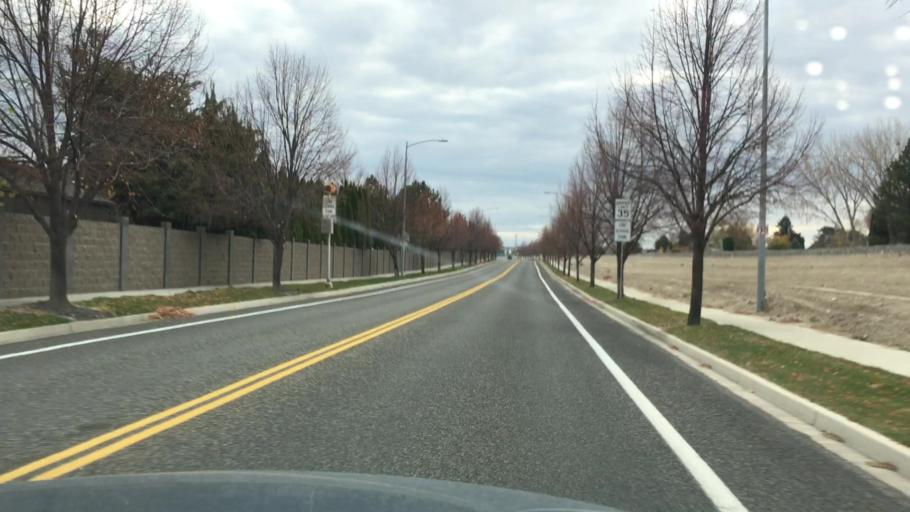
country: US
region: Washington
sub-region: Benton County
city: Kennewick
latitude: 46.1867
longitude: -119.1890
